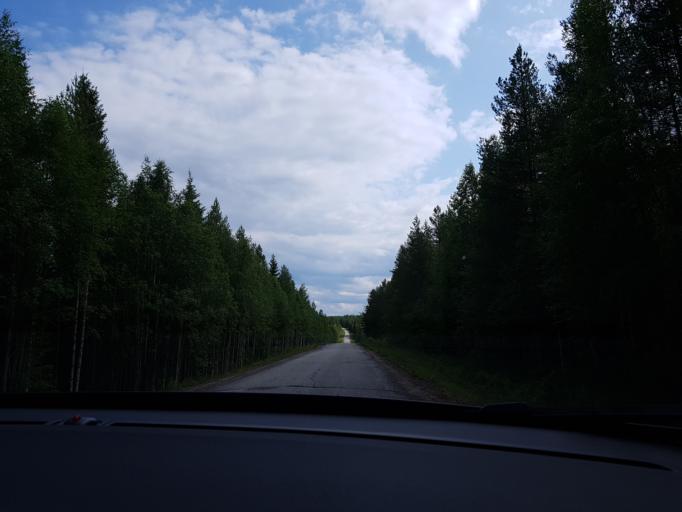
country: FI
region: Kainuu
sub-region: Kehys-Kainuu
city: Kuhmo
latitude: 64.4437
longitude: 29.7009
